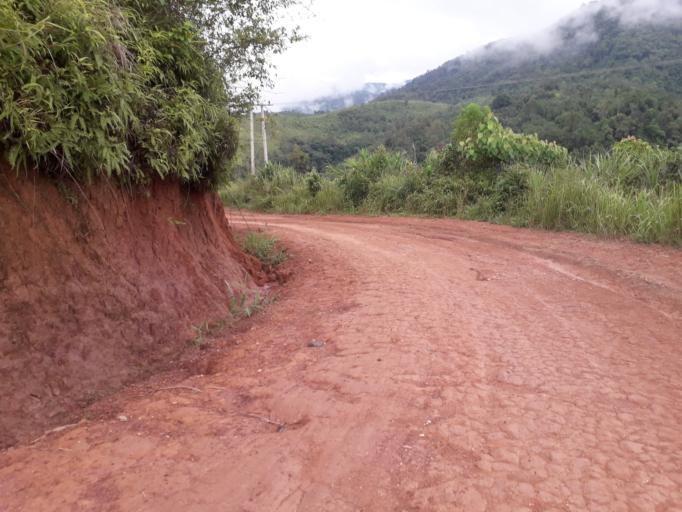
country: CN
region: Yunnan
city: Menglie
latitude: 22.2651
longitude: 101.5783
